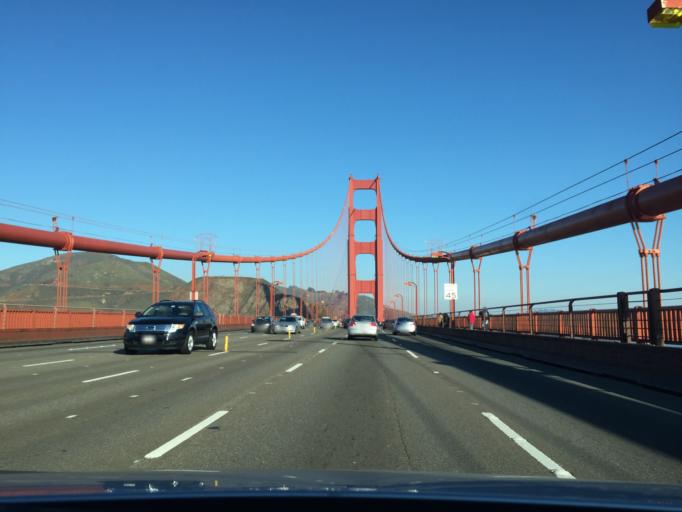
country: US
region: California
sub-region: Marin County
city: Sausalito
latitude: 37.8202
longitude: -122.4786
